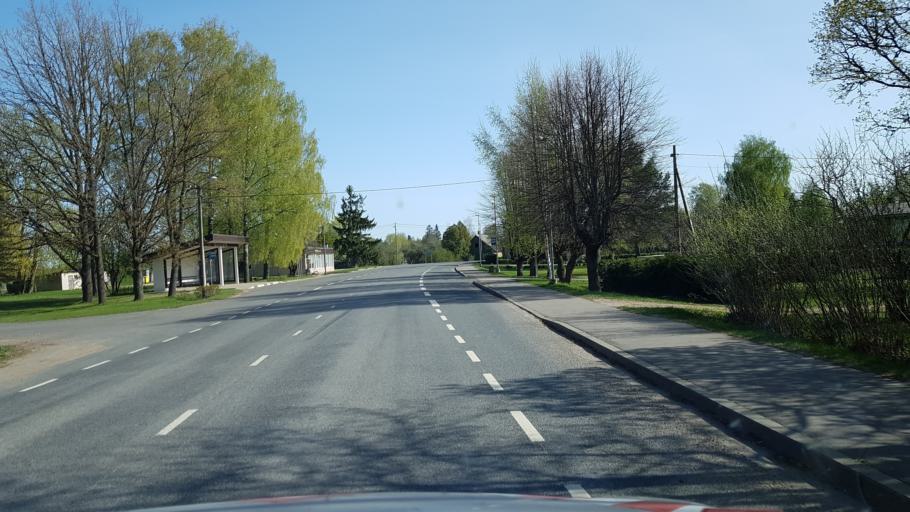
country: EE
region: Viljandimaa
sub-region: Abja vald
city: Abja-Paluoja
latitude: 58.1631
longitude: 25.4383
